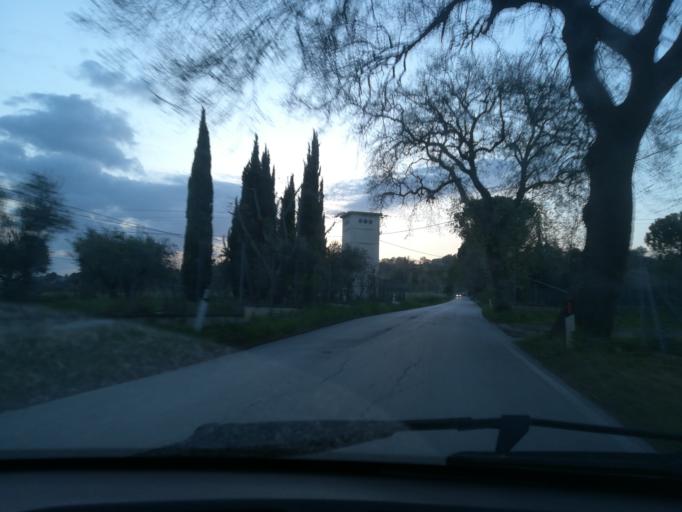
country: IT
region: The Marches
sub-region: Provincia di Macerata
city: Macerata
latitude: 43.2760
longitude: 13.4540
